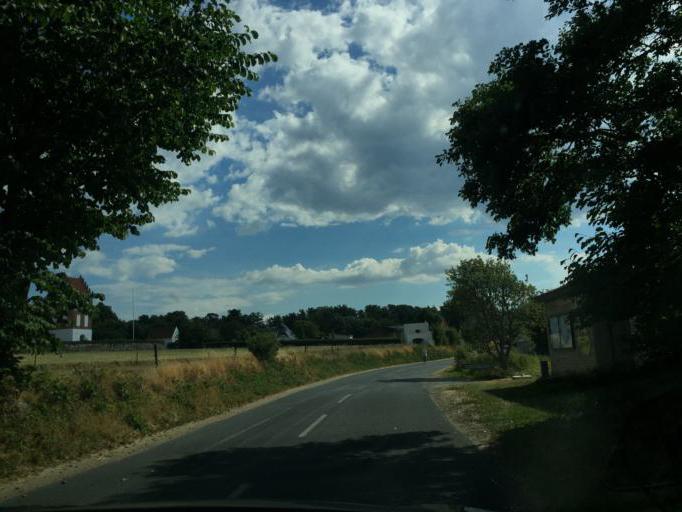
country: DK
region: South Denmark
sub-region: Assens Kommune
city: Harby
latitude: 55.1429
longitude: 10.0205
